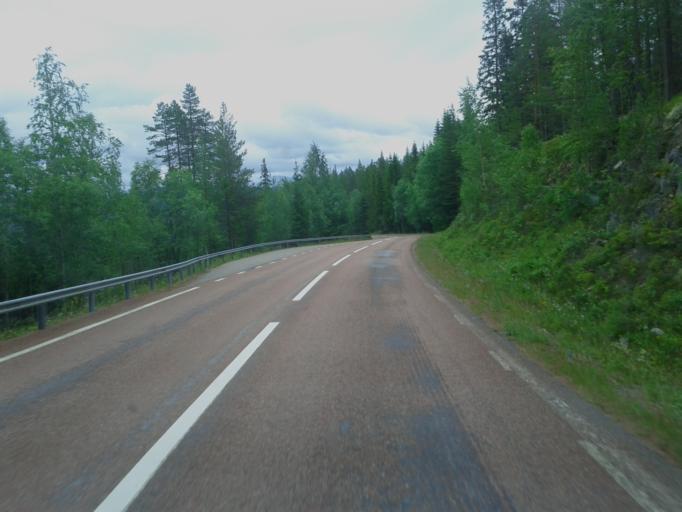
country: NO
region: Hedmark
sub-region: Trysil
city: Innbygda
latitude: 61.8500
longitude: 12.6101
